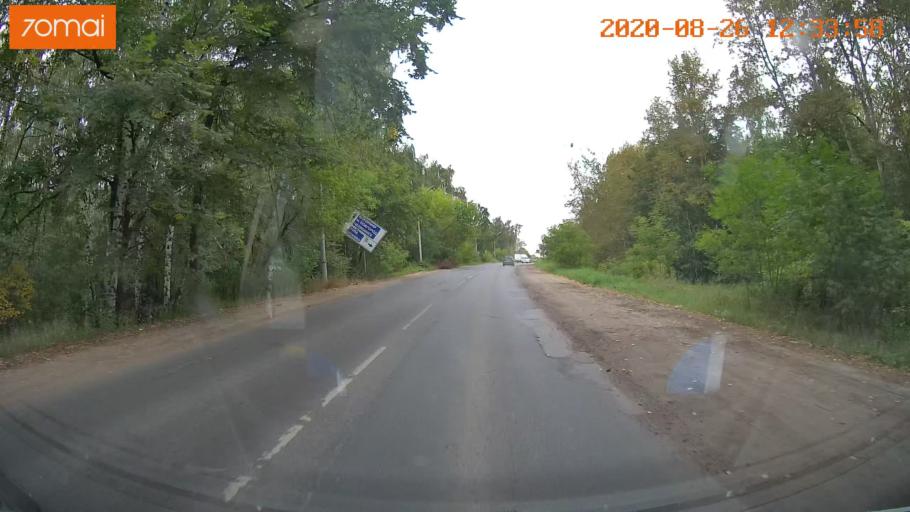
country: RU
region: Rjazan
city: Ryazan'
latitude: 54.5846
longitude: 39.7730
